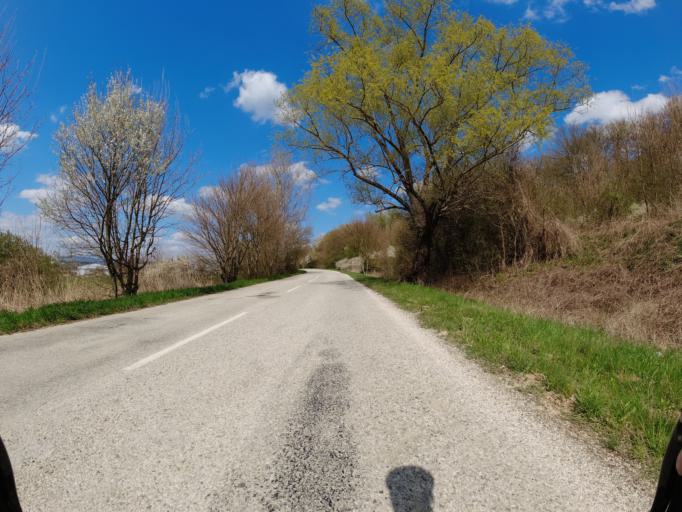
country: SK
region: Nitriansky
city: Stara Tura
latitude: 48.7282
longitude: 17.7226
